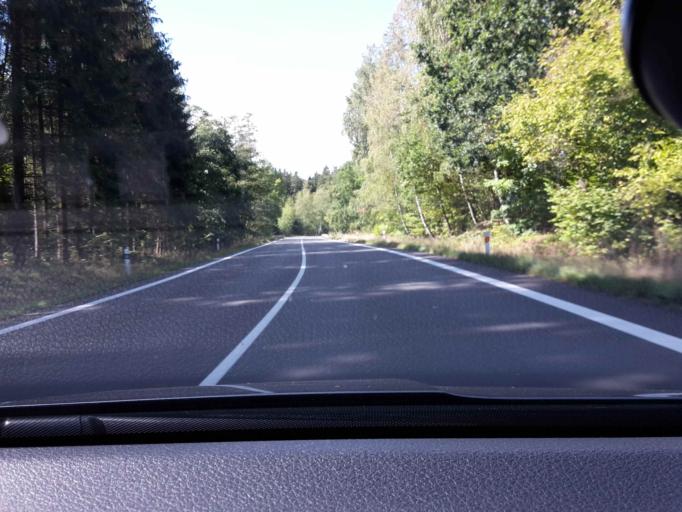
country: CZ
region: Jihocesky
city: Strmilov
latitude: 49.1796
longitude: 15.1385
